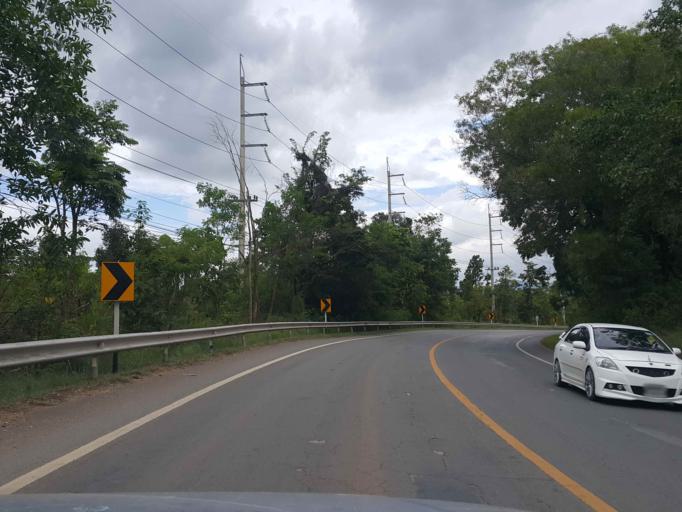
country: TH
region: Lamphun
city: Thung Hua Chang
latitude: 17.9746
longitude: 98.8773
